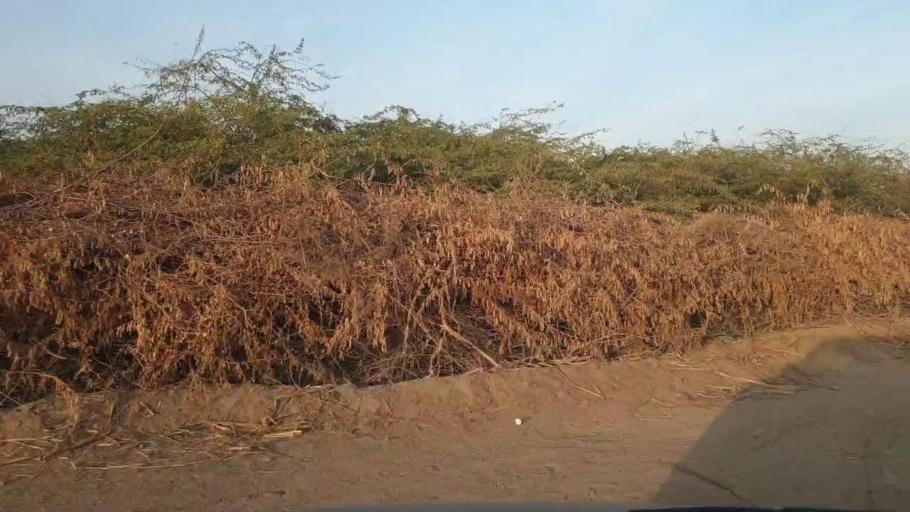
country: PK
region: Sindh
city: Chambar
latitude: 25.2804
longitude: 68.8396
